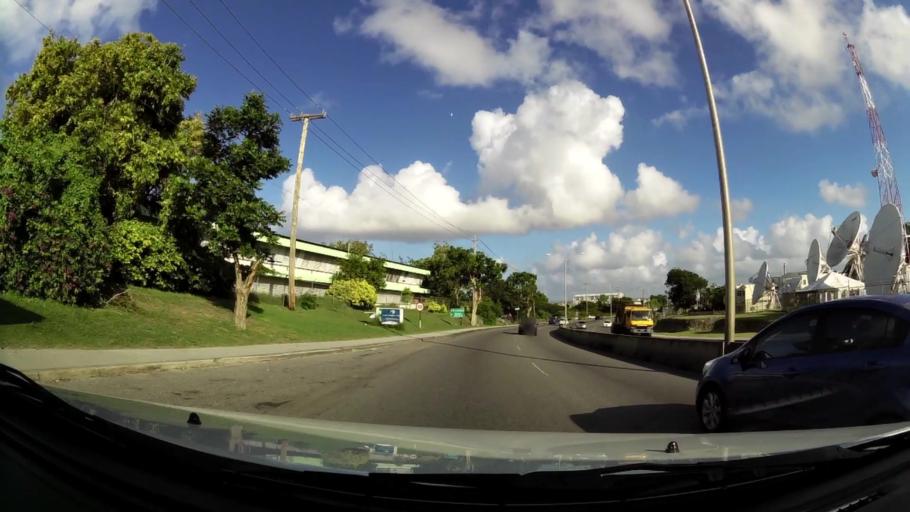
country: BB
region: Saint Michael
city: Bridgetown
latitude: 13.0980
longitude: -59.5799
